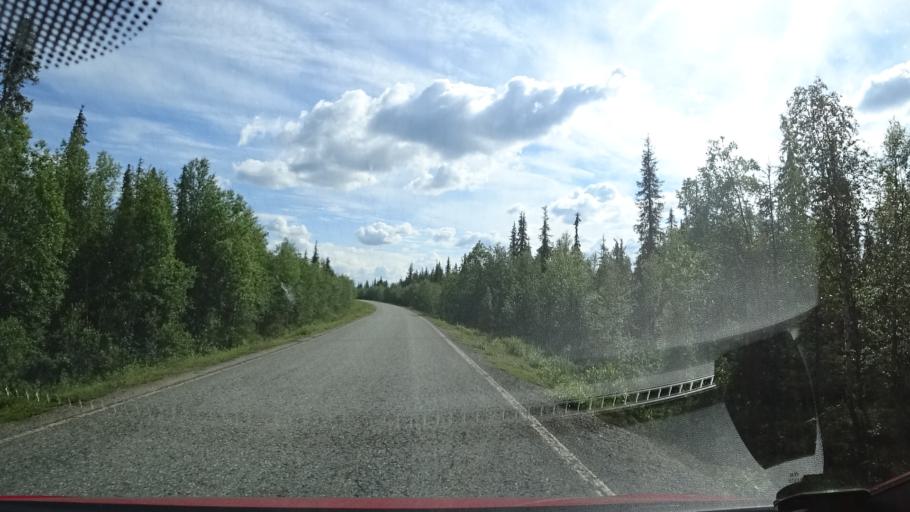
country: FI
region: Lapland
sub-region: Tunturi-Lappi
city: Kittilae
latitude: 68.2053
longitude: 25.7856
